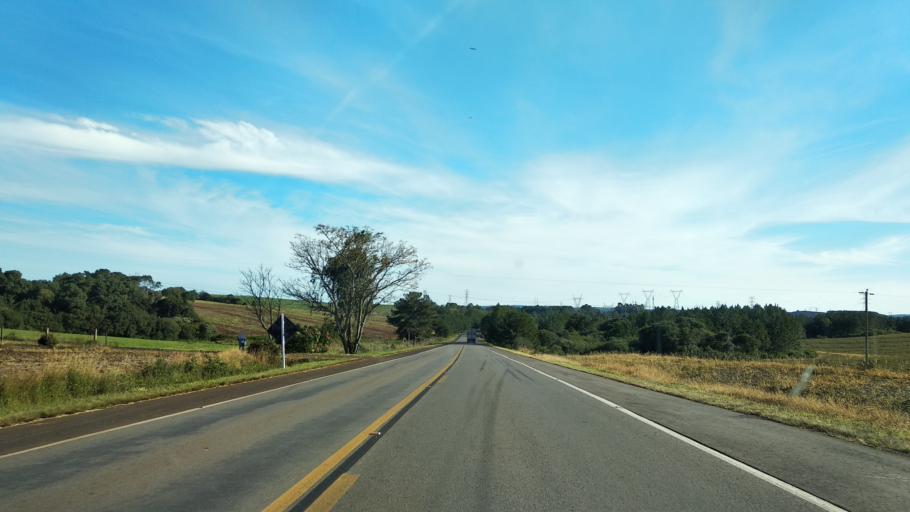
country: BR
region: Santa Catarina
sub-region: Celso Ramos
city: Celso Ramos
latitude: -27.5343
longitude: -51.4009
